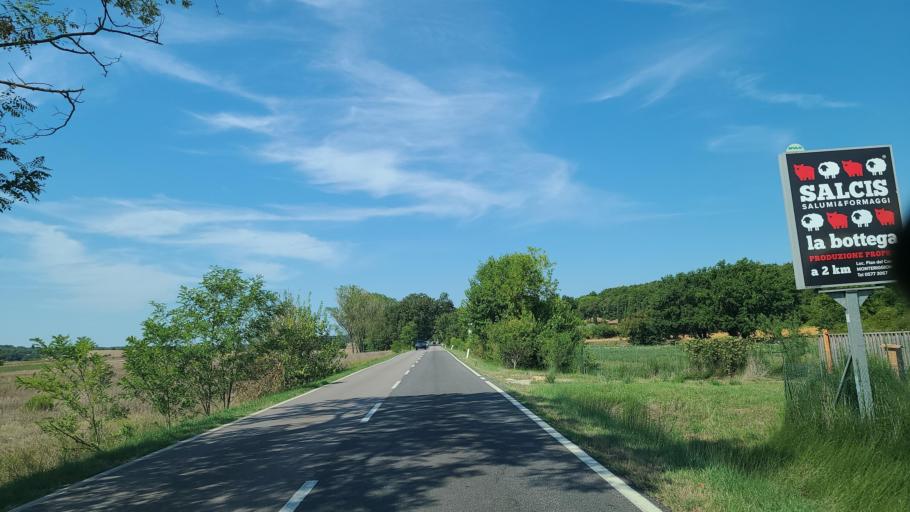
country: IT
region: Tuscany
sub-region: Provincia di Siena
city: Castellina Scalo
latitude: 43.3928
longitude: 11.2104
